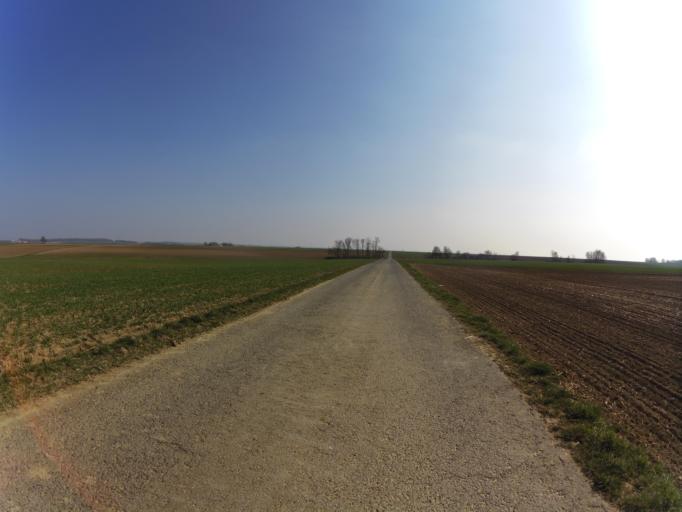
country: DE
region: Bavaria
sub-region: Regierungsbezirk Unterfranken
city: Gaukonigshofen
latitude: 49.6560
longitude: 9.9889
